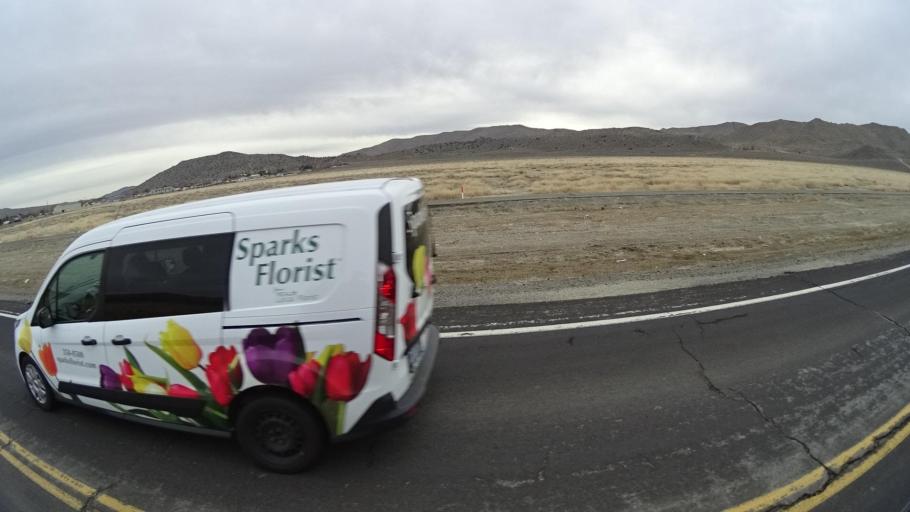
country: US
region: Nevada
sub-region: Washoe County
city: Lemmon Valley
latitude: 39.6556
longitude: -119.8285
